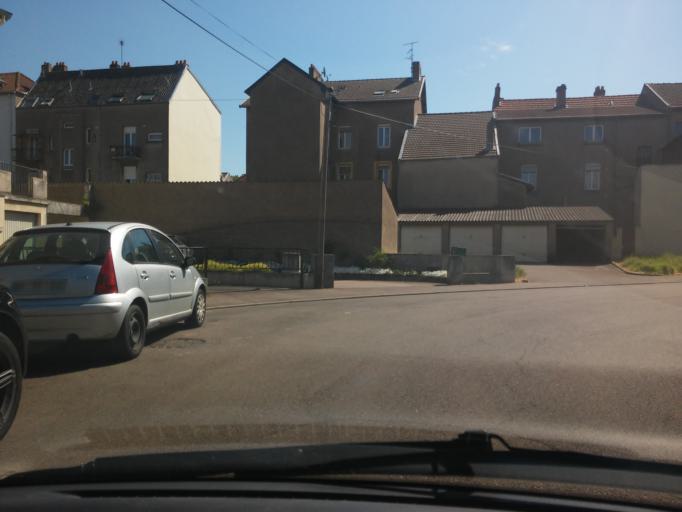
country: FR
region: Lorraine
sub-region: Departement de la Moselle
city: Hagondange
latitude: 49.2453
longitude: 6.1692
